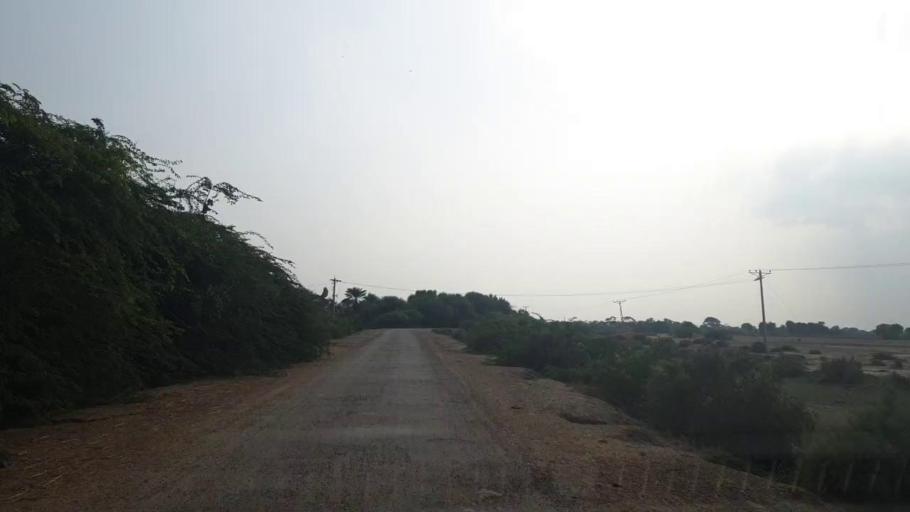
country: PK
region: Sindh
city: Badin
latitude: 24.6391
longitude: 68.6937
